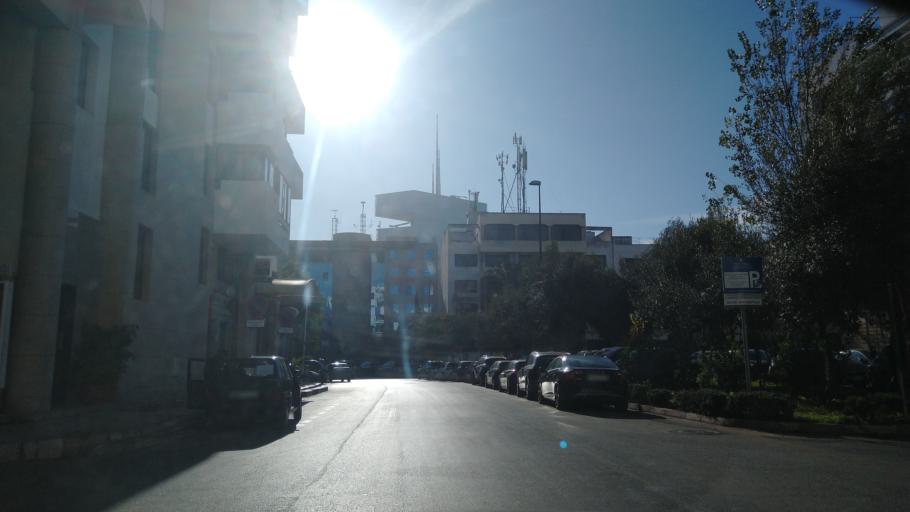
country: MA
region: Rabat-Sale-Zemmour-Zaer
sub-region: Skhirate-Temara
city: Temara
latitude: 33.9608
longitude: -6.8680
